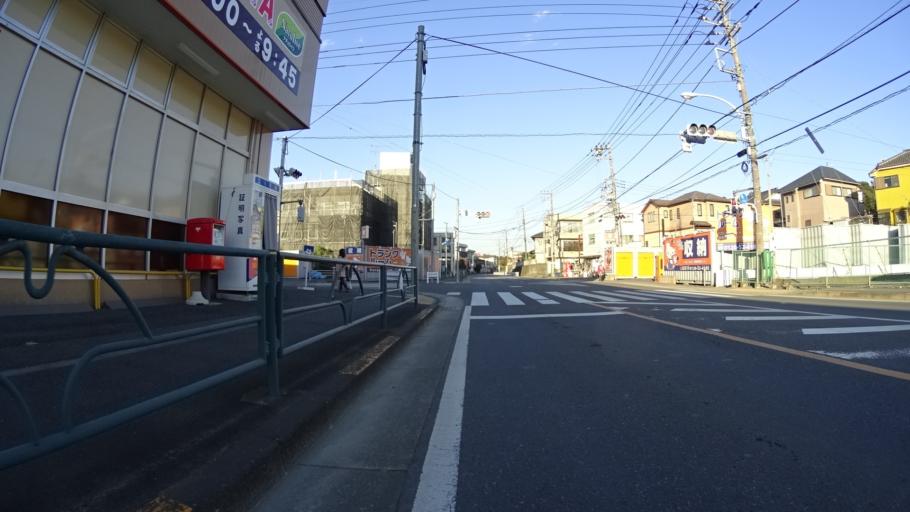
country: JP
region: Tokyo
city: Hachioji
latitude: 35.6780
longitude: 139.2705
